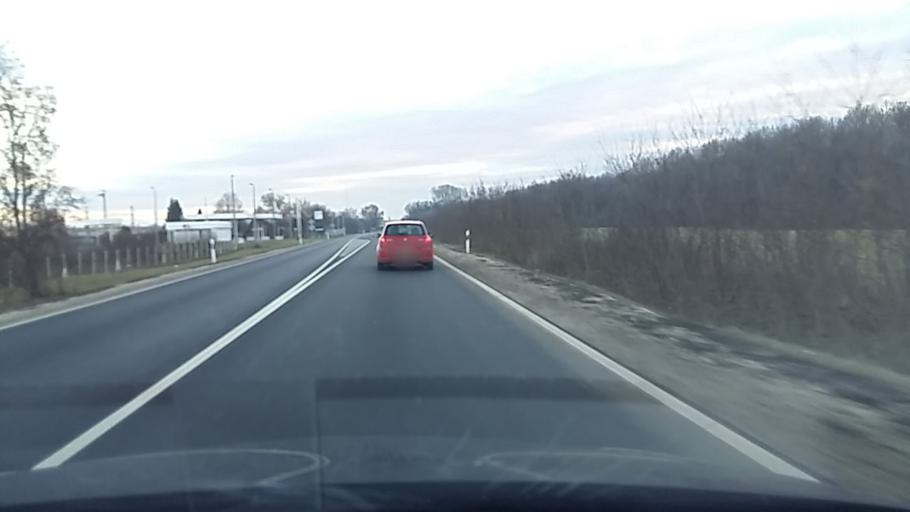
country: HU
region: Hajdu-Bihar
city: Debrecen
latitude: 47.5879
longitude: 21.6545
